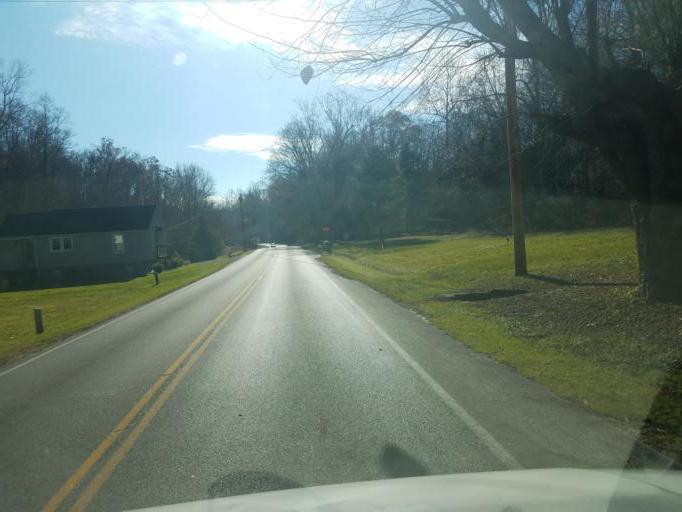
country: US
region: Ohio
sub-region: Scioto County
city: Sciotodale
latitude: 38.8342
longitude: -82.8512
